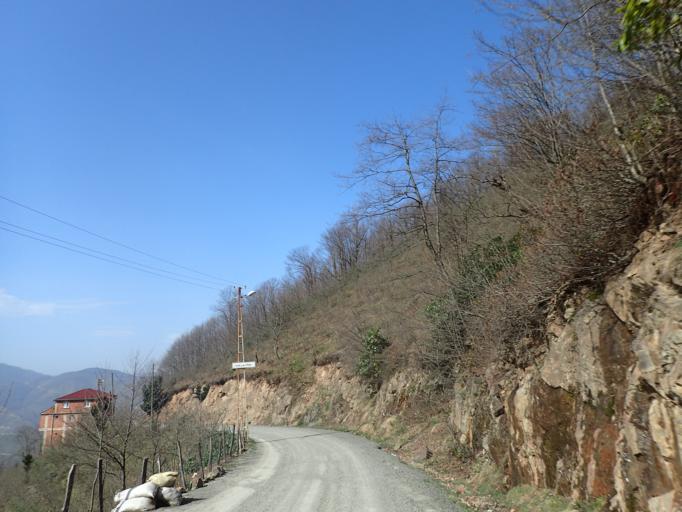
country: TR
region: Ordu
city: Kabaduz
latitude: 40.8247
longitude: 37.8891
